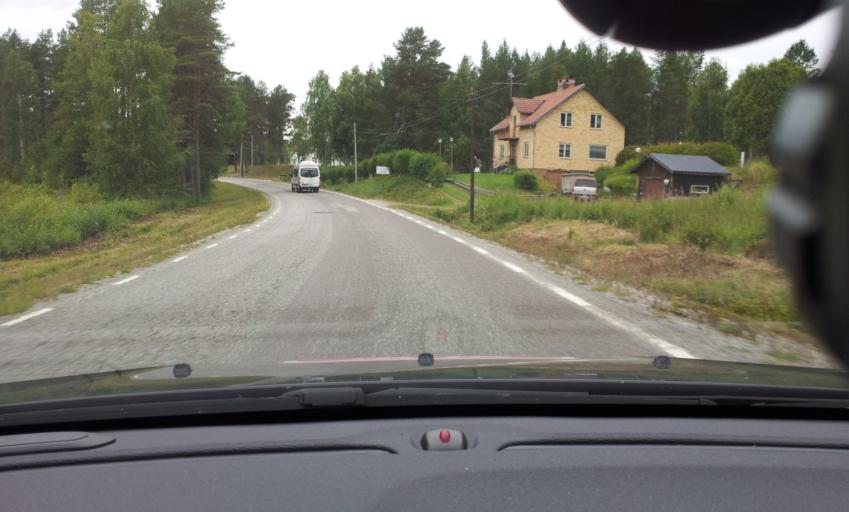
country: SE
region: Jaemtland
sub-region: Braecke Kommun
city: Braecke
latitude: 63.0174
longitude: 15.2159
